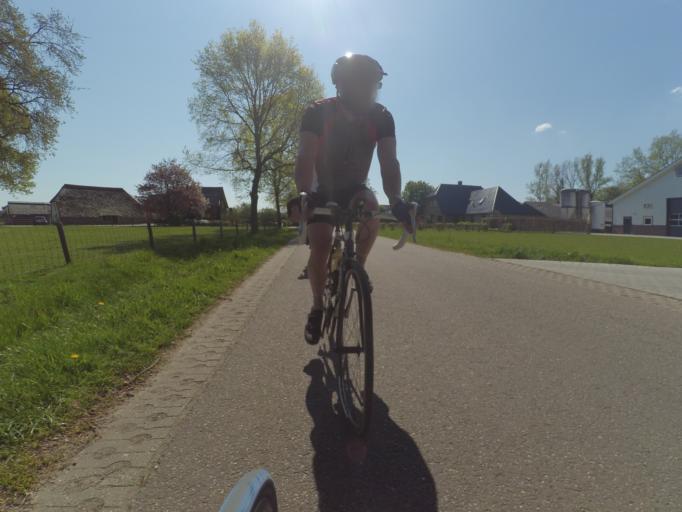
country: NL
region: Gelderland
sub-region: Gemeente Apeldoorn
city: Uddel
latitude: 52.2612
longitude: 5.7759
